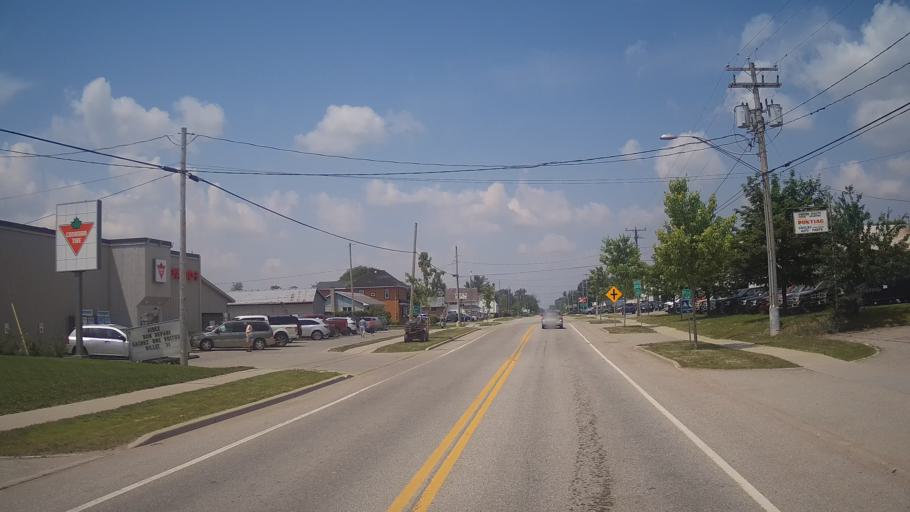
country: CA
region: Quebec
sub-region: Outaouais
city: Shawville
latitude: 45.5988
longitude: -76.4914
